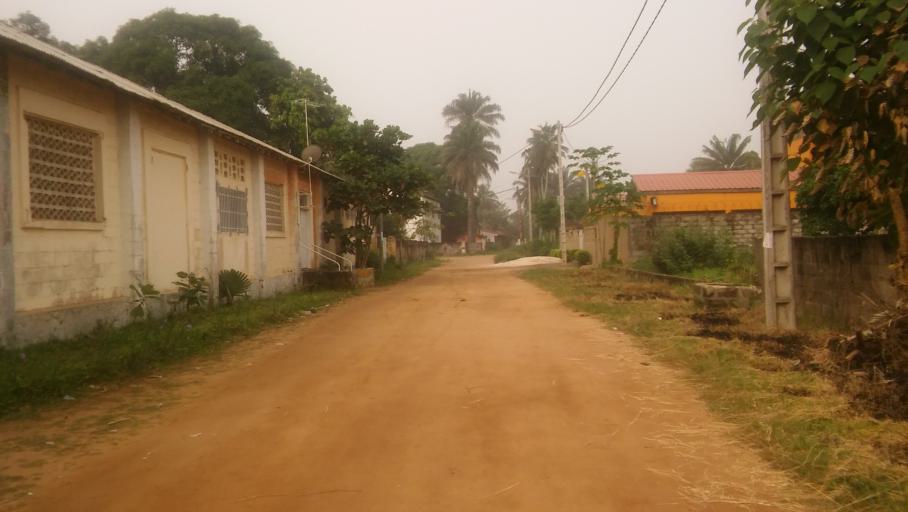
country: CI
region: Sud-Comoe
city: Grand-Bassam
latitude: 5.1972
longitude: -3.7398
